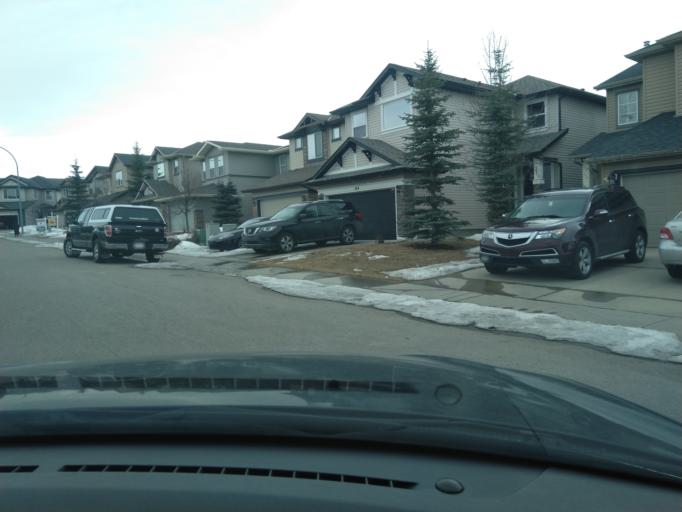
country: CA
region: Alberta
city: Calgary
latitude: 51.1581
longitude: -114.0900
